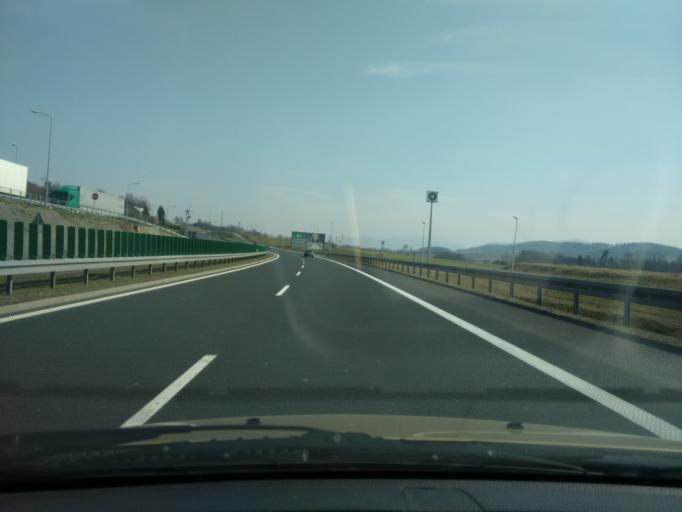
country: PL
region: Silesian Voivodeship
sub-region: Powiat cieszynski
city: Bazanowice
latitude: 49.7650
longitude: 18.7016
